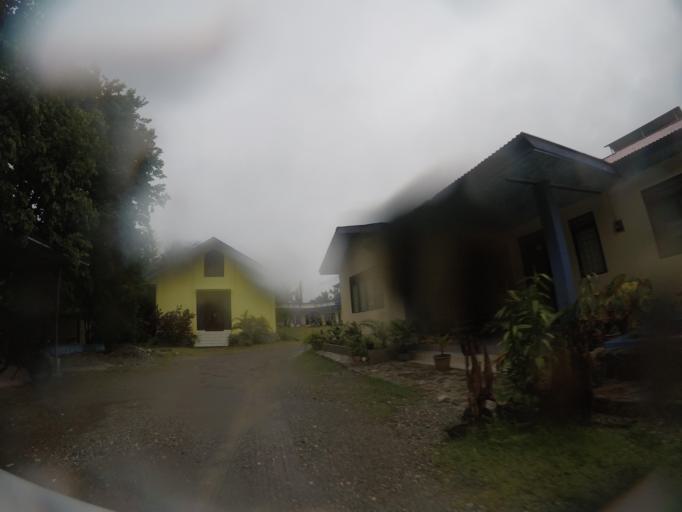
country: TL
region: Bobonaro
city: Maliana
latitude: -8.9949
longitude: 125.2263
